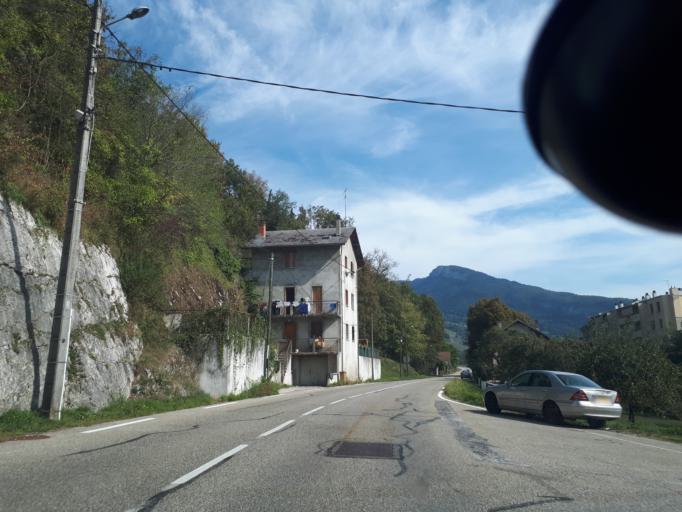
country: FR
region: Rhone-Alpes
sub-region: Departement de la Savoie
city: Les Echelles
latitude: 45.4387
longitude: 5.7571
